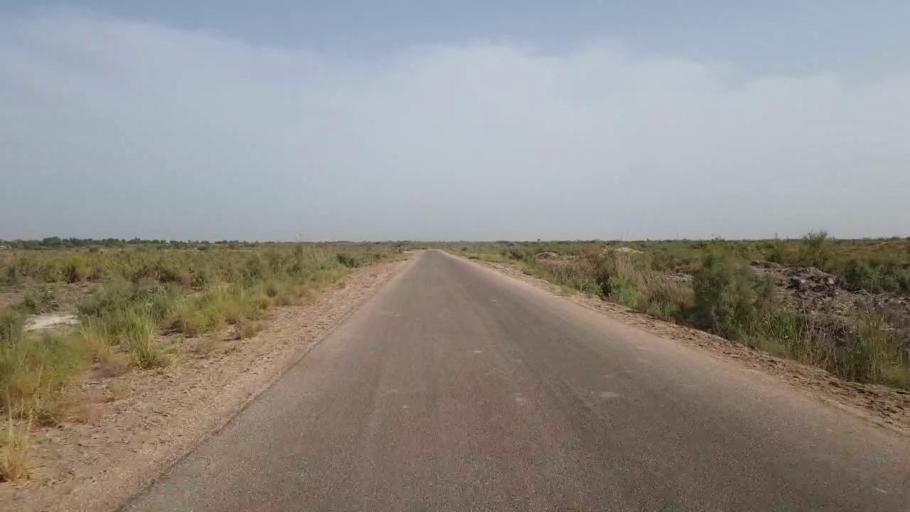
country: PK
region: Sindh
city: Sakrand
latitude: 26.2754
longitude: 68.2717
